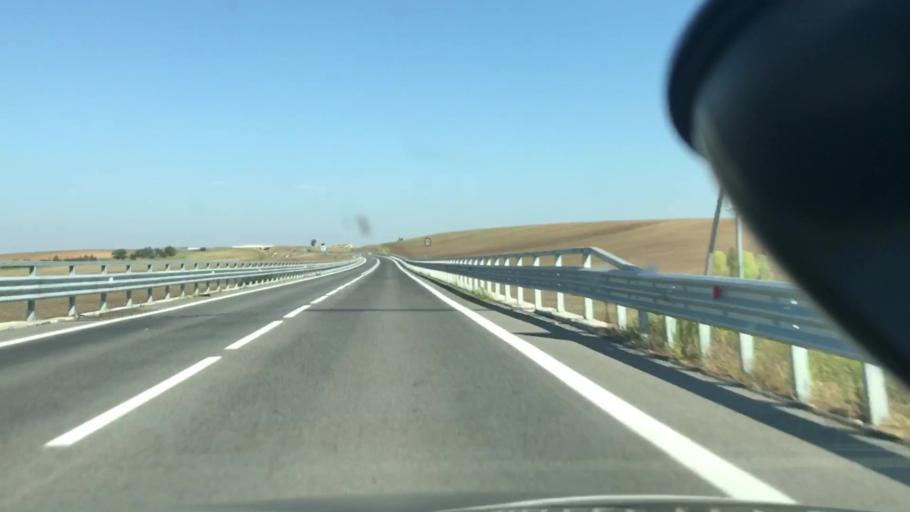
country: IT
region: Basilicate
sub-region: Provincia di Potenza
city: Palazzo San Gervasio
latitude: 40.9616
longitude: 16.0125
